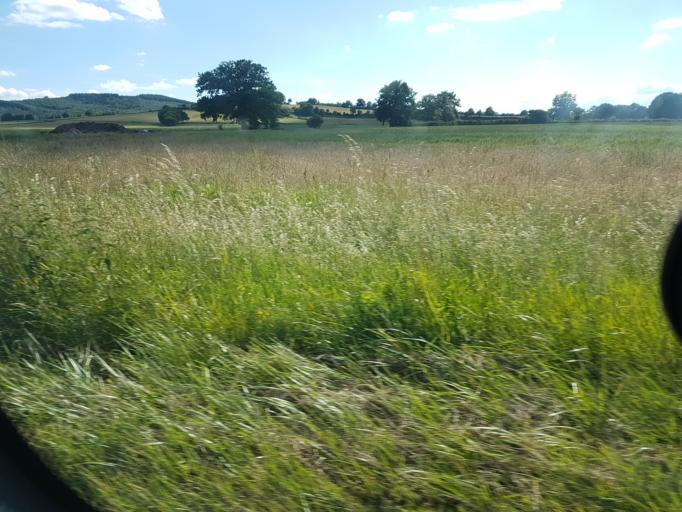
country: FR
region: Bourgogne
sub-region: Departement de Saone-et-Loire
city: Epinac
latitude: 46.9965
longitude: 4.4800
